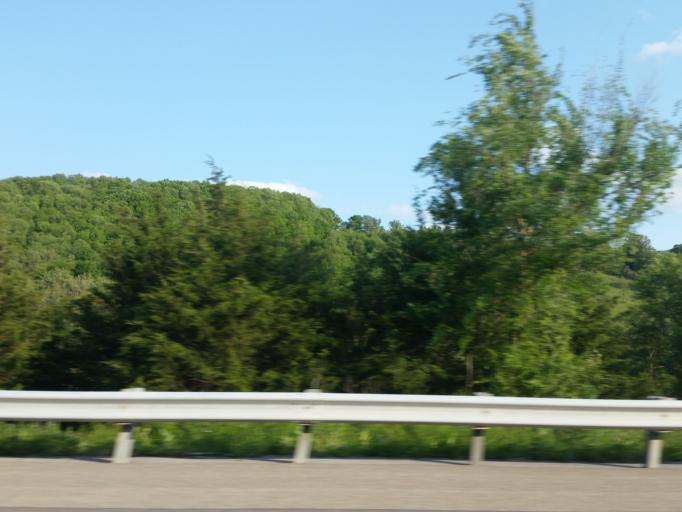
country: US
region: Virginia
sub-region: Tazewell County
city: Raven
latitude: 36.9918
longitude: -81.8421
